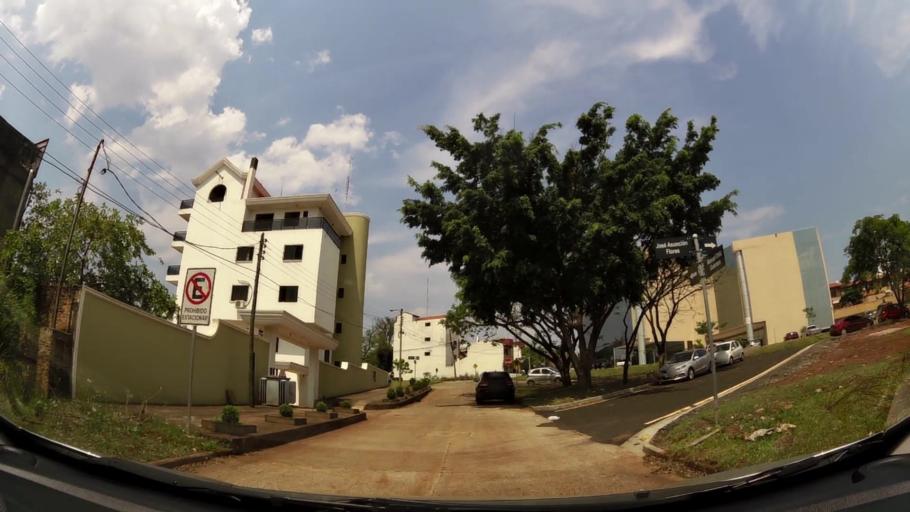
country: PY
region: Alto Parana
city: Ciudad del Este
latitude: -25.4790
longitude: -54.6249
